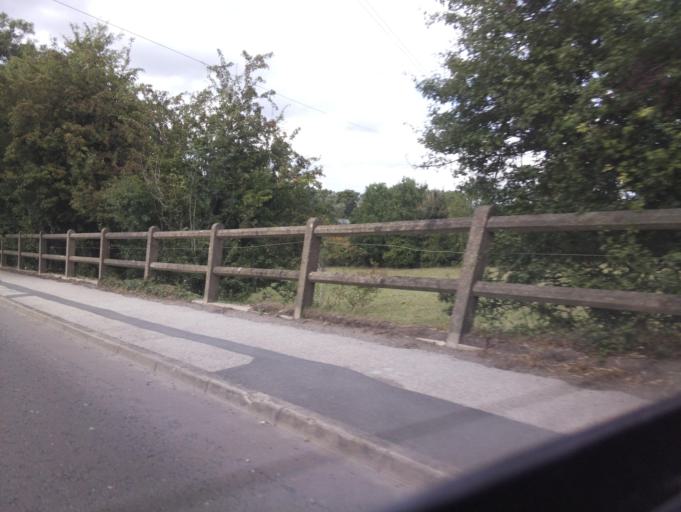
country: GB
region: England
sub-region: North Yorkshire
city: Harrogate
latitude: 54.0125
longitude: -1.5557
